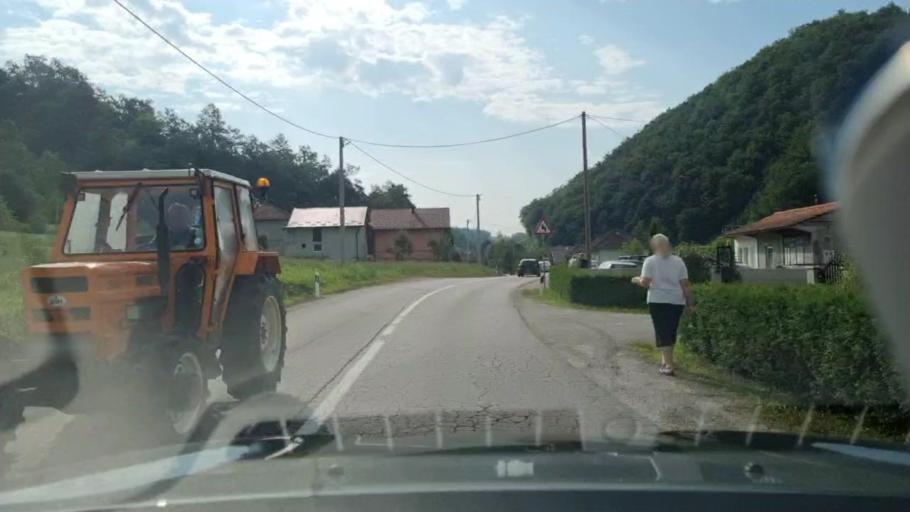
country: BA
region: Federation of Bosnia and Herzegovina
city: Jezerski
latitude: 45.0239
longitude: 16.0815
